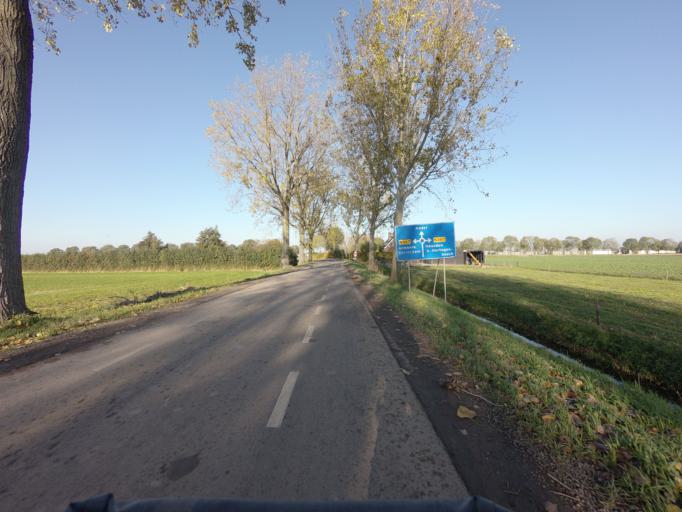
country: NL
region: North Brabant
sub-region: Gemeente Woudrichem
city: Woudrichem
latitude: 51.7715
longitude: 5.0489
